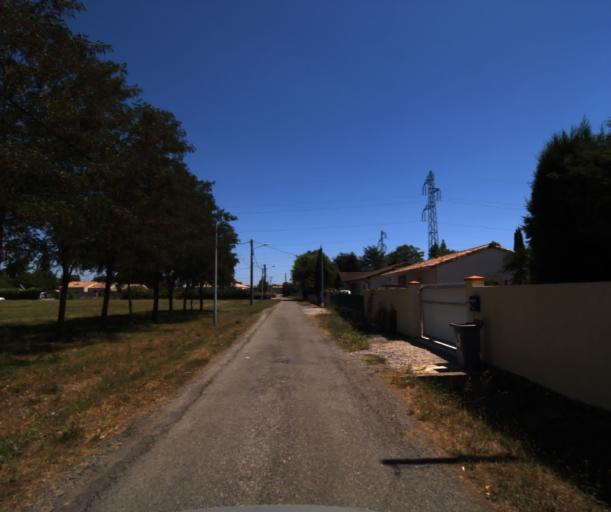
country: FR
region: Midi-Pyrenees
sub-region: Departement de la Haute-Garonne
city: Seysses
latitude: 43.4641
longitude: 1.3103
